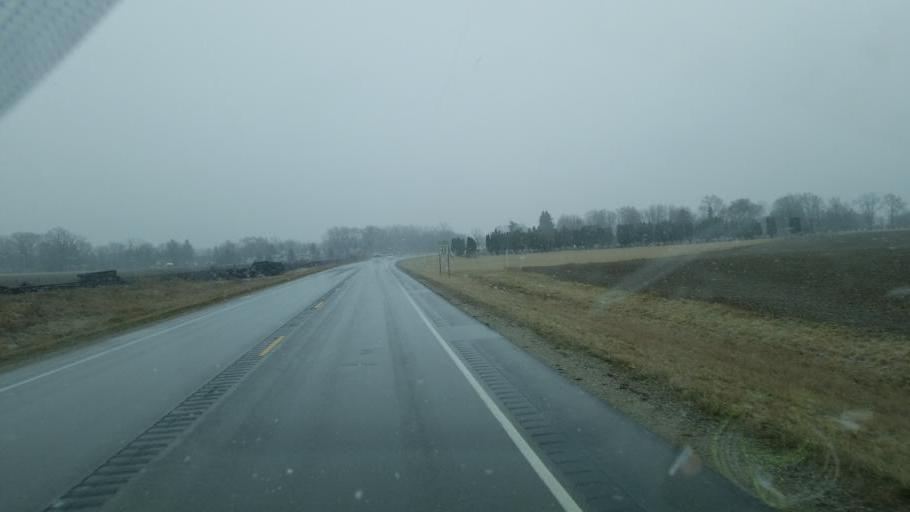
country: US
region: Indiana
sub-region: Wabash County
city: Mount Vernon
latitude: 40.6781
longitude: -85.7295
